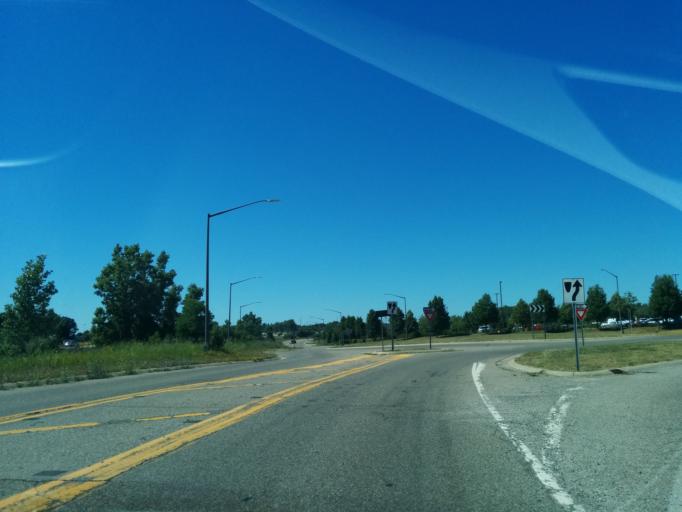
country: US
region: Michigan
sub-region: Oakland County
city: Walled Lake
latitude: 42.5348
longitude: -83.4479
